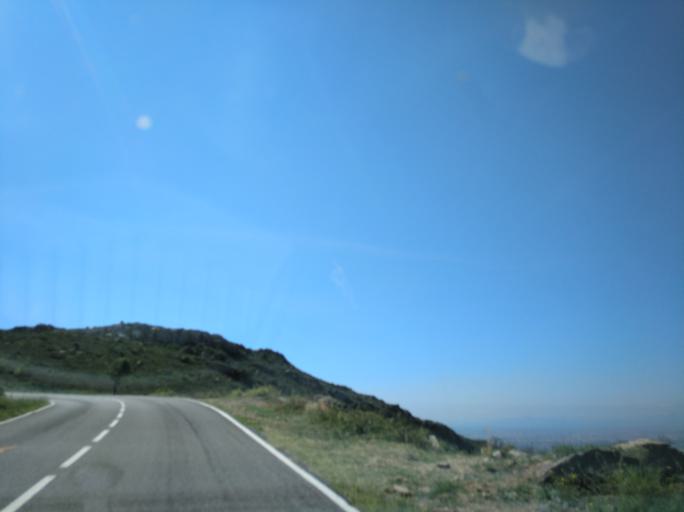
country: ES
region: Catalonia
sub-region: Provincia de Girona
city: Pau
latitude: 42.3275
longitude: 3.1404
